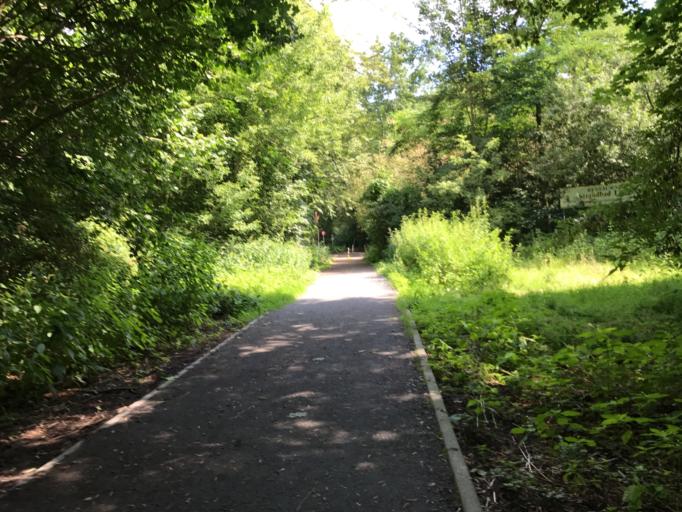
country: DE
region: Brandenburg
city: Glienicke
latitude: 52.6188
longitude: 13.3324
